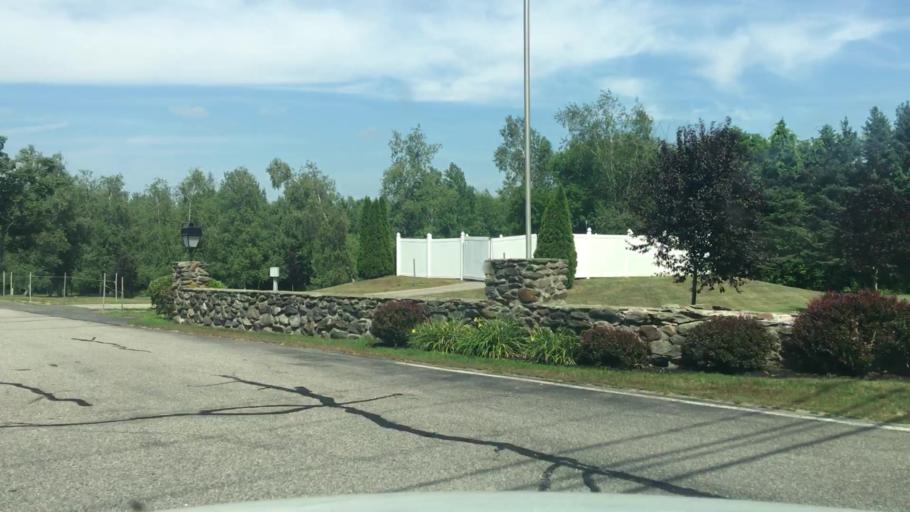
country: US
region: New Hampshire
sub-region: Strafford County
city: Rochester
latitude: 43.3129
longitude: -70.9315
